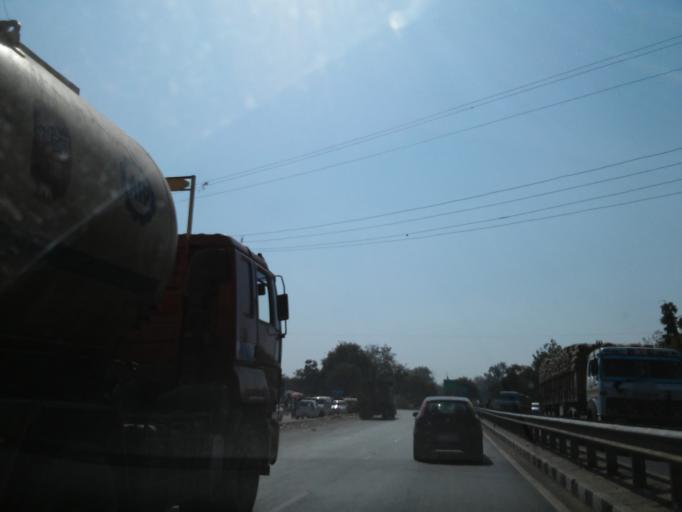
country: IN
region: Gujarat
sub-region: Gandhinagar
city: Ghandinagar
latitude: 23.2284
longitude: 72.7315
